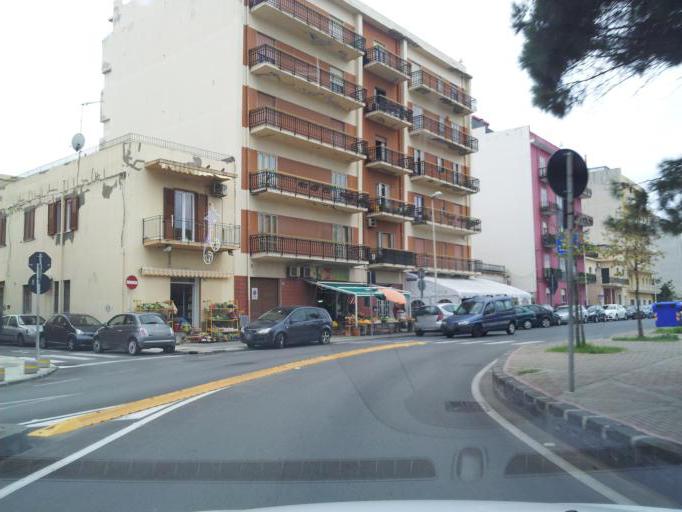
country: IT
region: Sicily
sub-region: Messina
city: Milazzo
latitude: 38.2261
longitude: 15.2384
